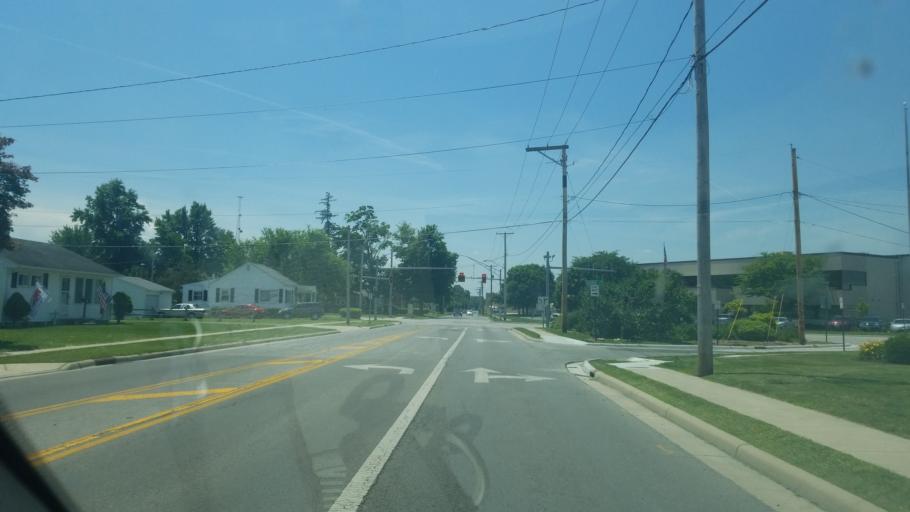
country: US
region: Ohio
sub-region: Hancock County
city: Findlay
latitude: 41.0543
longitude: -83.6409
